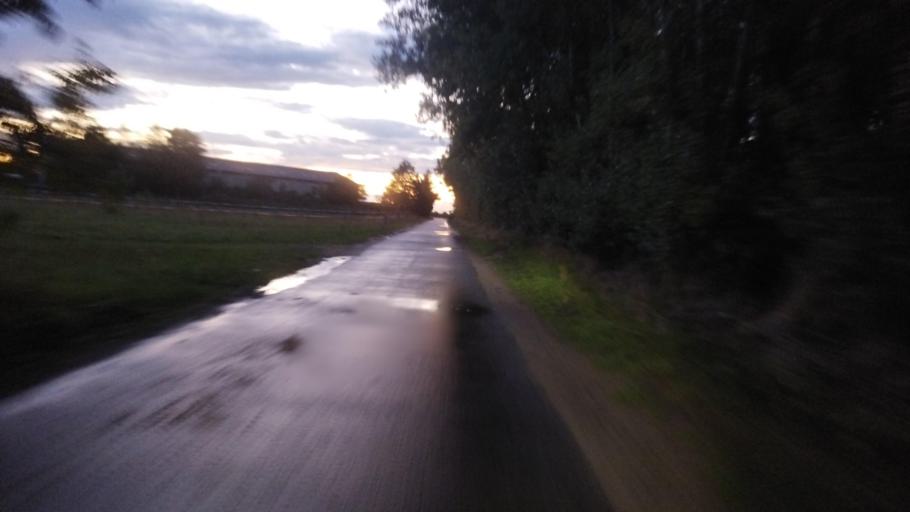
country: DE
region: Hesse
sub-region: Regierungsbezirk Darmstadt
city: Einhausen
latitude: 49.6781
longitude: 8.5316
